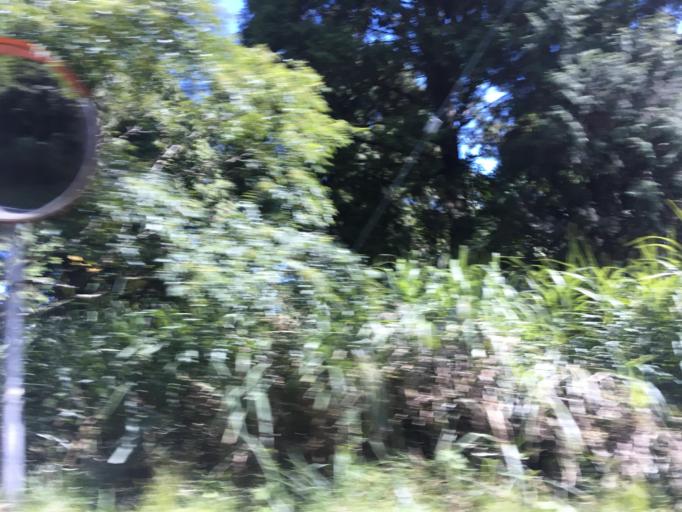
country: TW
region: Taiwan
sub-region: Yilan
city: Yilan
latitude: 24.5225
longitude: 121.5194
